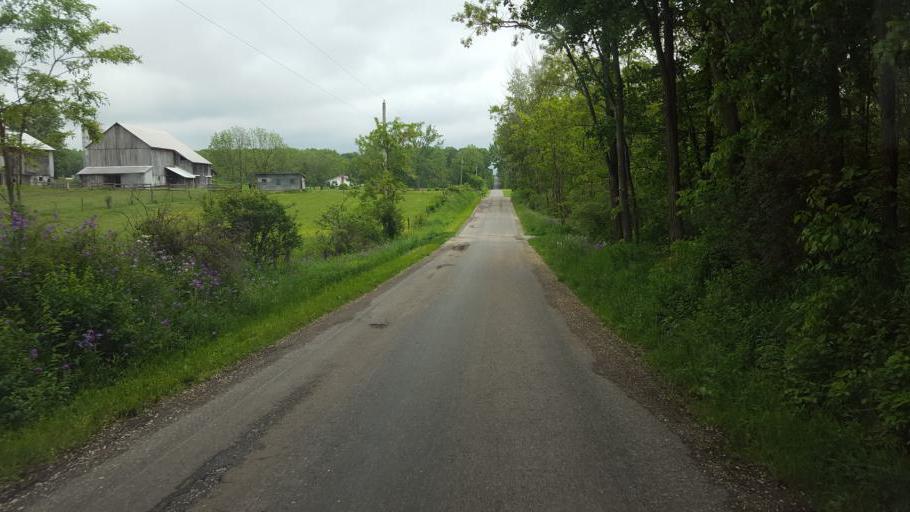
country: US
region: Ohio
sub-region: Wayne County
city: West Salem
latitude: 40.9377
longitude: -82.1802
